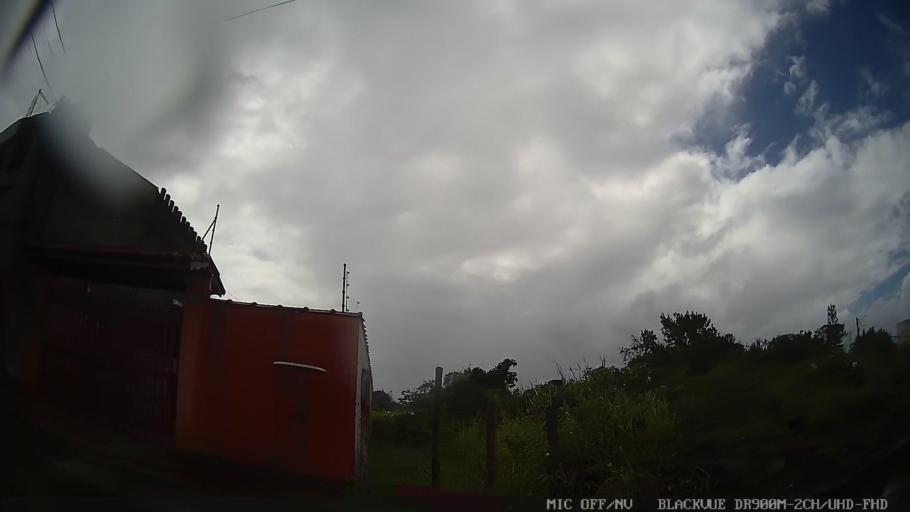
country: BR
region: Sao Paulo
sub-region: Itanhaem
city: Itanhaem
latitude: -24.2316
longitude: -46.9031
